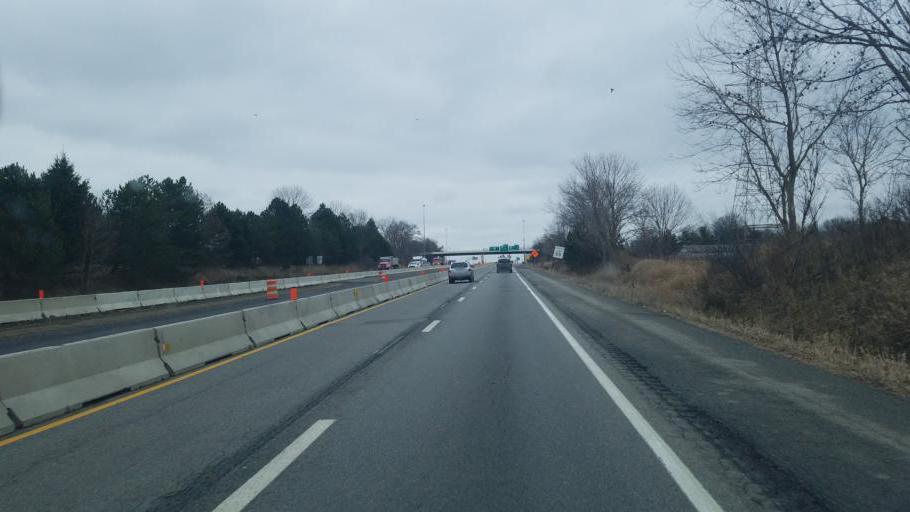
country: US
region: Ohio
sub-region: Summit County
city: Norton
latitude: 41.0400
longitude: -81.6715
